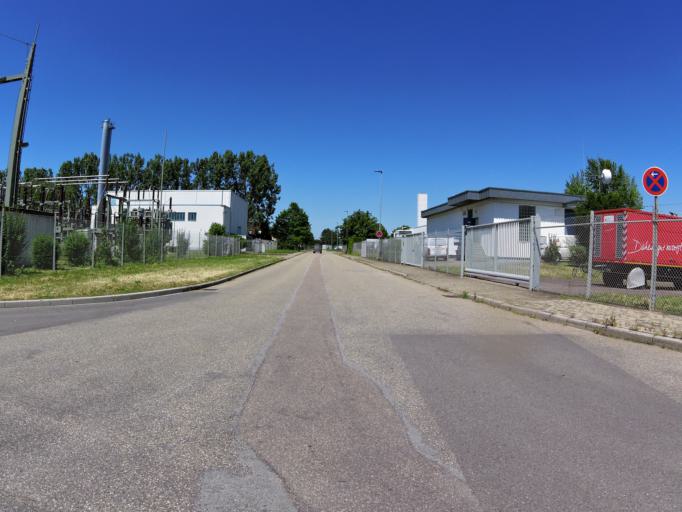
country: DE
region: Baden-Wuerttemberg
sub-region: Freiburg Region
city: Kippenheim
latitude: 48.3426
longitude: 7.8214
